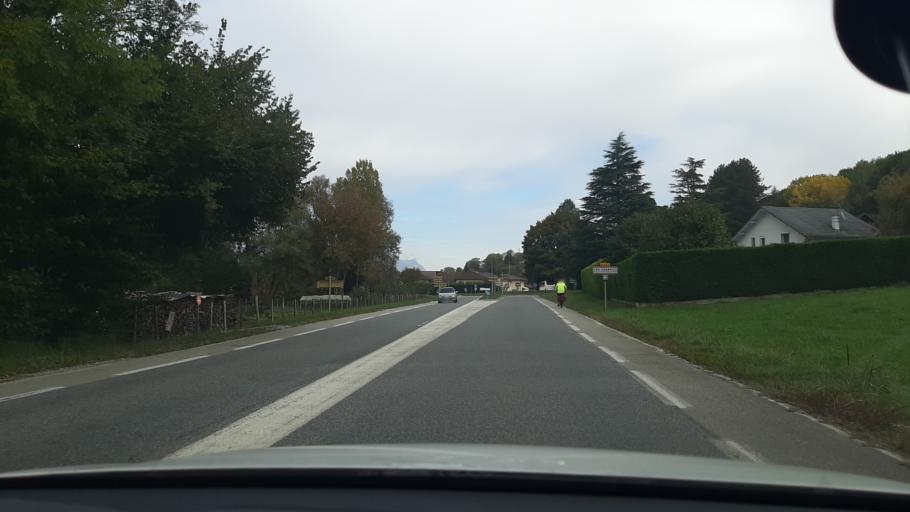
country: FR
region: Rhone-Alpes
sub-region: Departement de la Savoie
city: Montmelian
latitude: 45.4588
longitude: 6.0498
